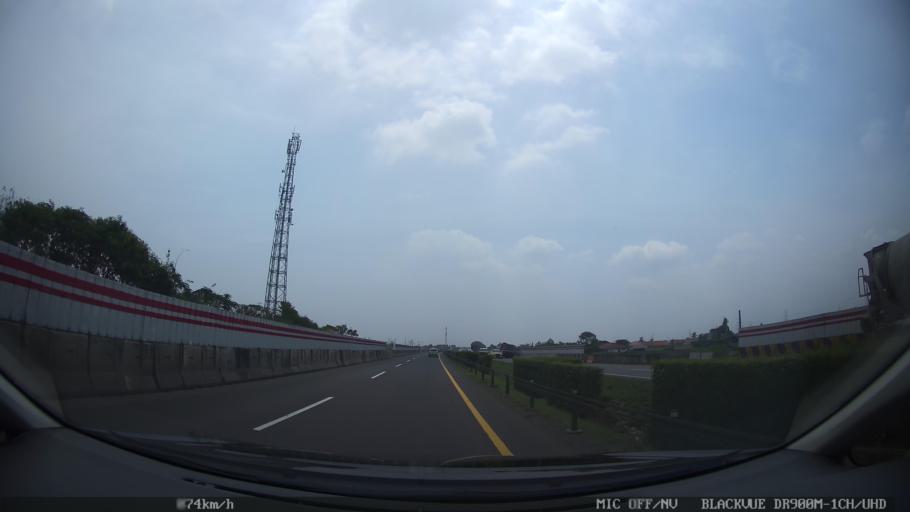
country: ID
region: West Java
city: Kresek
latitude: -6.1651
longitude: 106.3346
